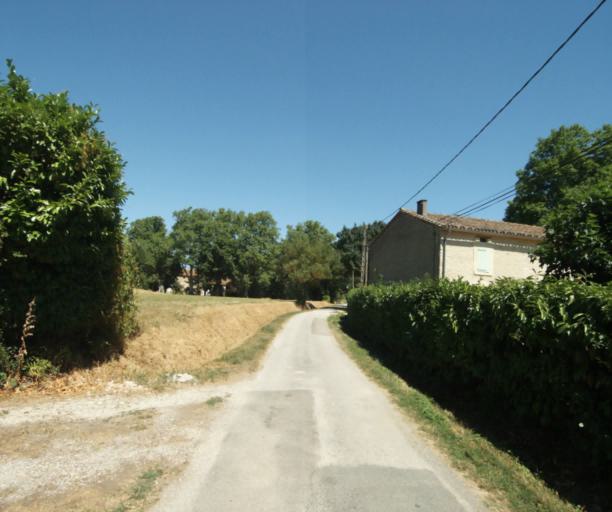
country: FR
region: Midi-Pyrenees
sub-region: Departement de la Haute-Garonne
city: Saint-Felix-Lauragais
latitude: 43.4787
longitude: 1.9429
